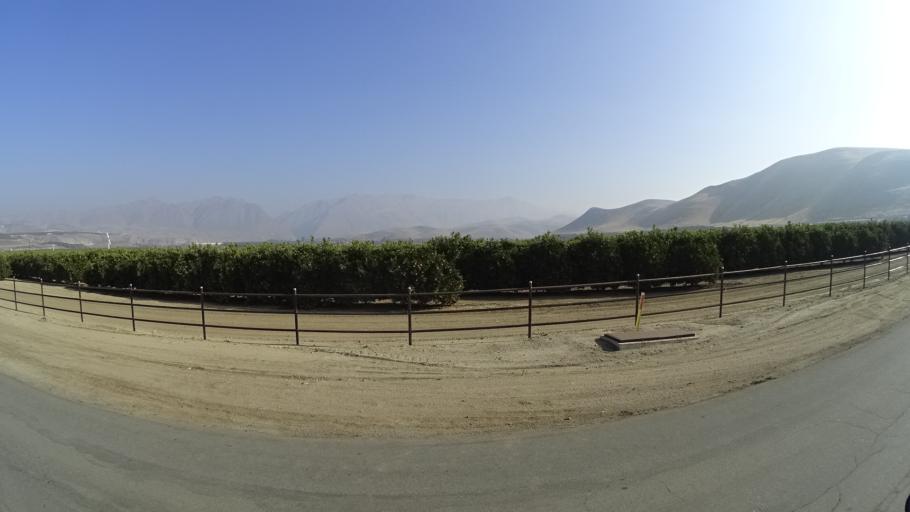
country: US
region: California
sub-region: Kern County
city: Lamont
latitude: 35.4182
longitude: -118.8324
